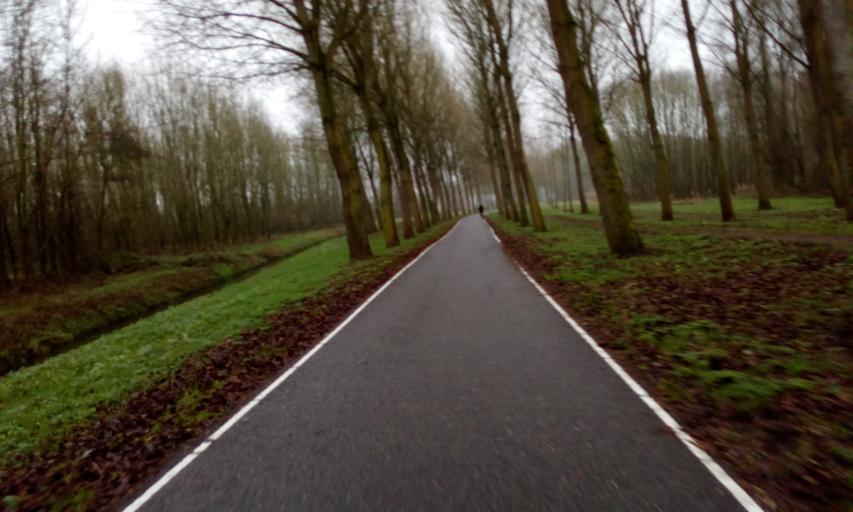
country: NL
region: South Holland
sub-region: Gemeente Den Haag
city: Ypenburg
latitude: 52.0281
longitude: 4.3891
